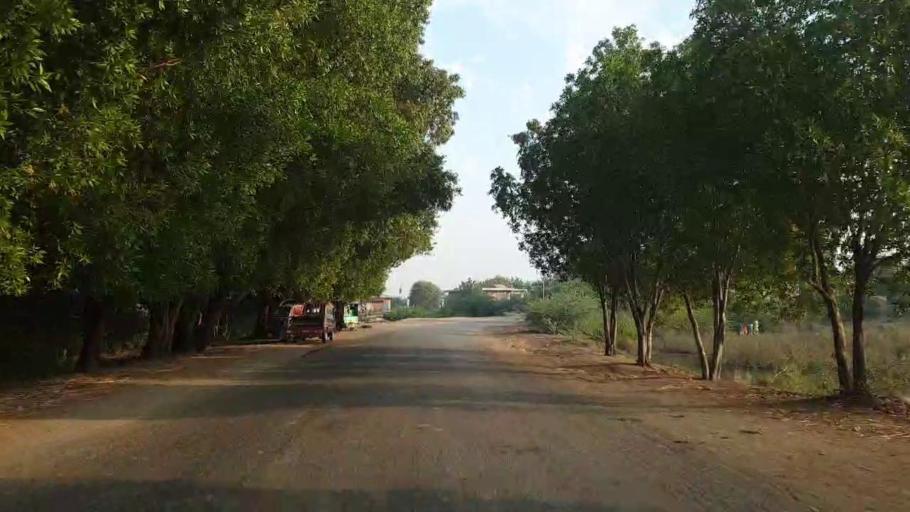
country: PK
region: Sindh
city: Tando Bago
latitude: 24.7190
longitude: 68.9401
